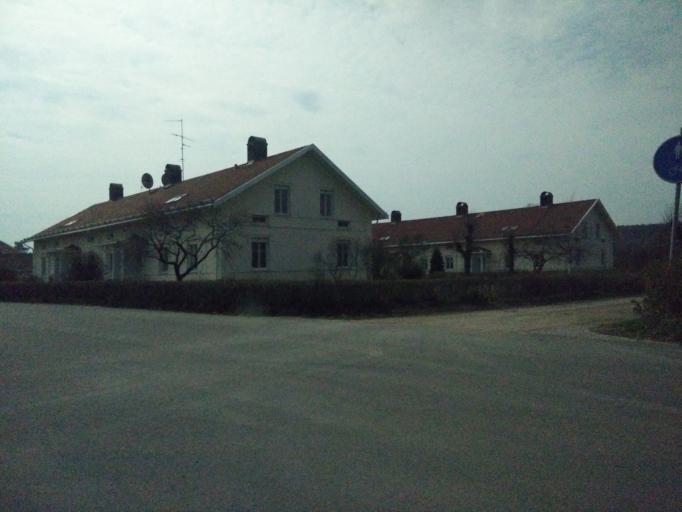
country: SE
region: Vaermland
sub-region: Munkfors Kommun
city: Munkfors
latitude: 59.8405
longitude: 13.5426
